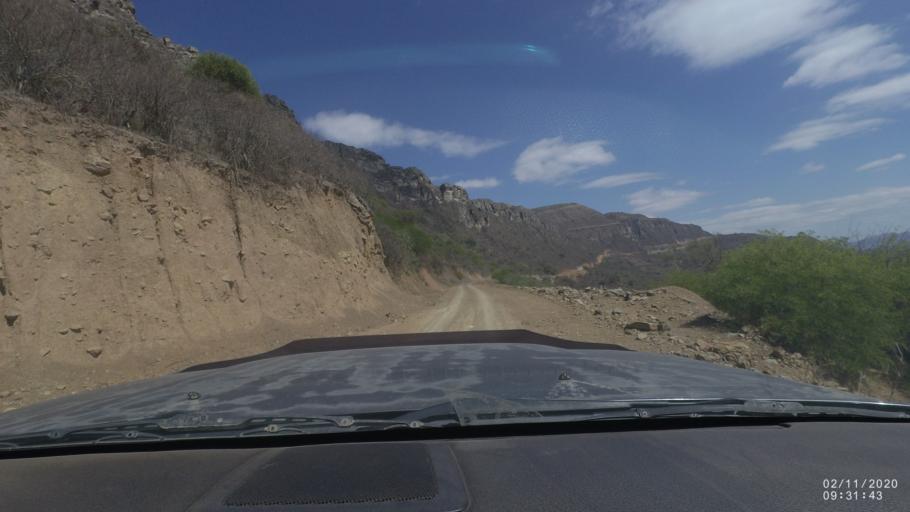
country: BO
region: Chuquisaca
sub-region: Provincia Zudanez
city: Mojocoya
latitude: -18.4261
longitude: -64.5843
